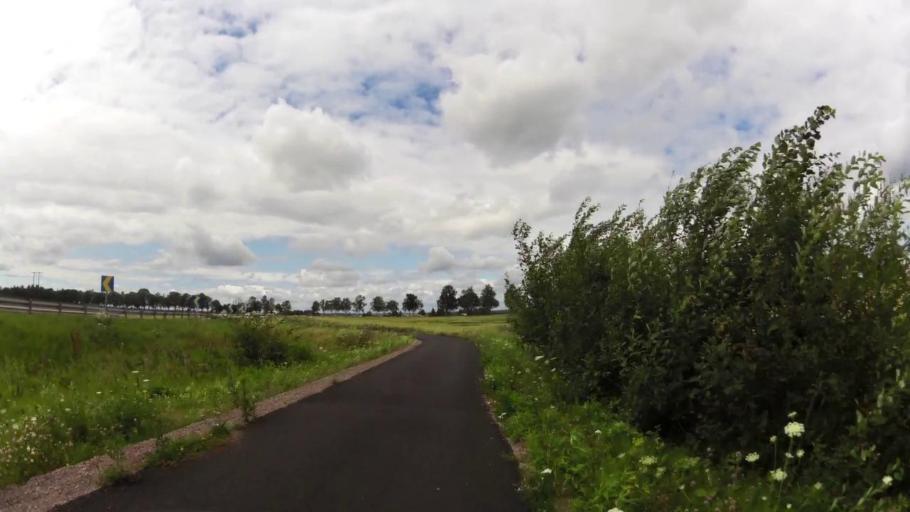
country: SE
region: OEstergoetland
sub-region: Linkopings Kommun
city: Berg
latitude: 58.4450
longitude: 15.5697
